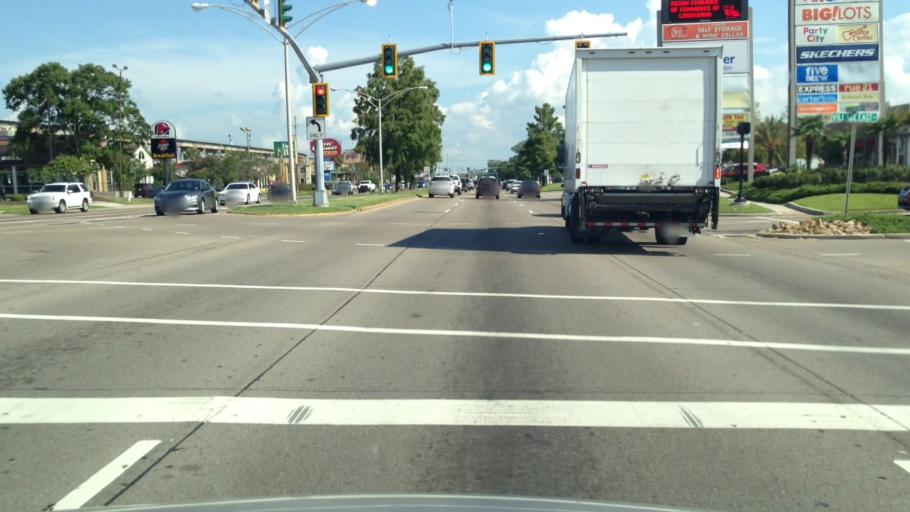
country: US
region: Louisiana
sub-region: Jefferson Parish
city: Elmwood
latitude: 29.9610
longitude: -90.1842
